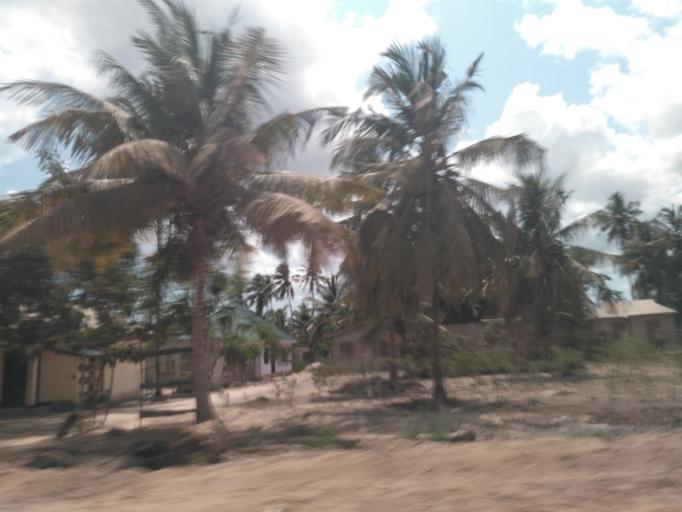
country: TZ
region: Dar es Salaam
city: Dar es Salaam
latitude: -6.8817
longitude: 39.3369
